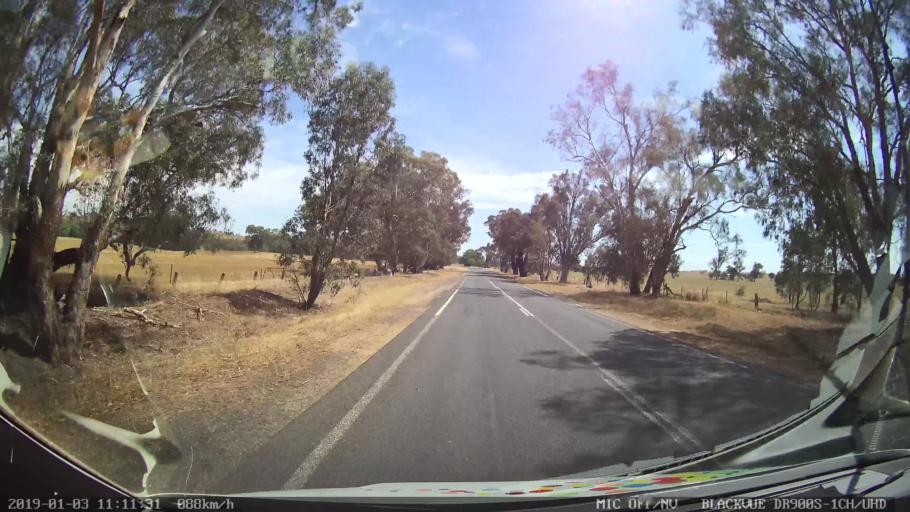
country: AU
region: New South Wales
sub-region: Young
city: Young
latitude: -34.2136
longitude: 148.2601
